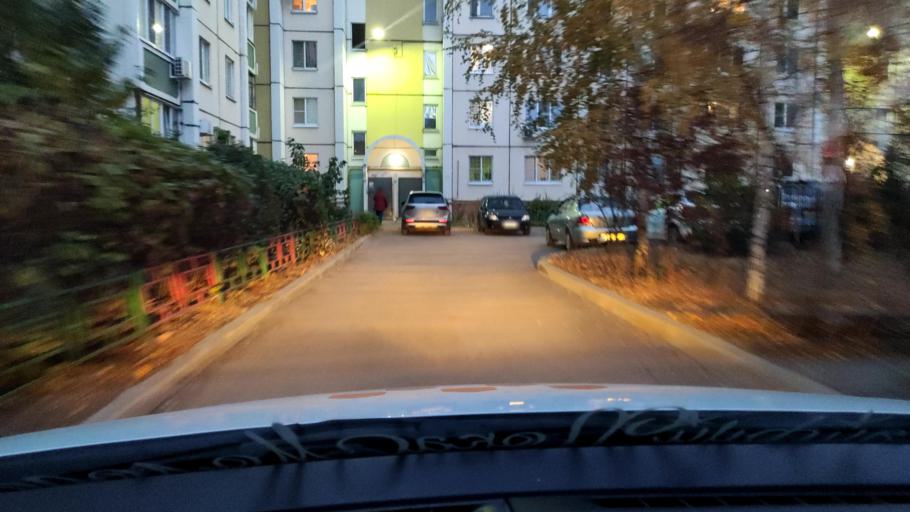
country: RU
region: Voronezj
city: Podgornoye
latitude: 51.7221
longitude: 39.1662
